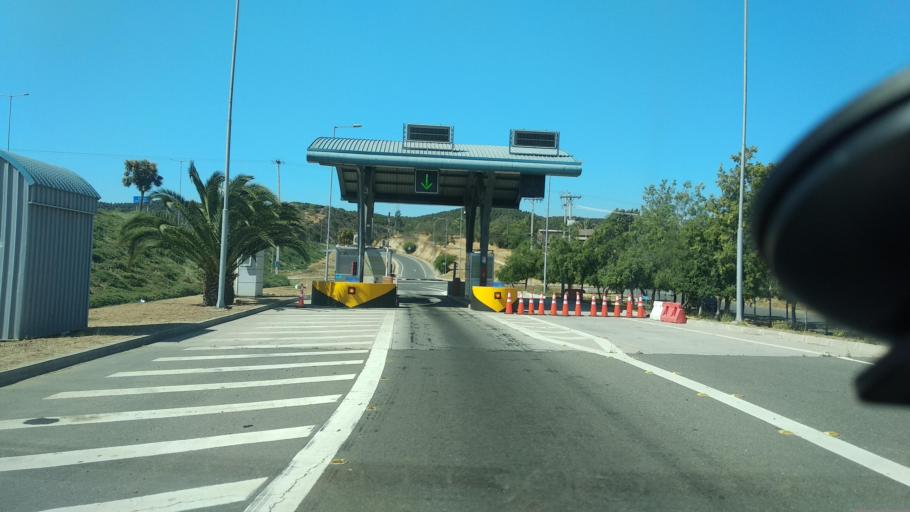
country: CL
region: Valparaiso
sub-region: Provincia de Marga Marga
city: Limache
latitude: -32.9725
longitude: -71.3012
